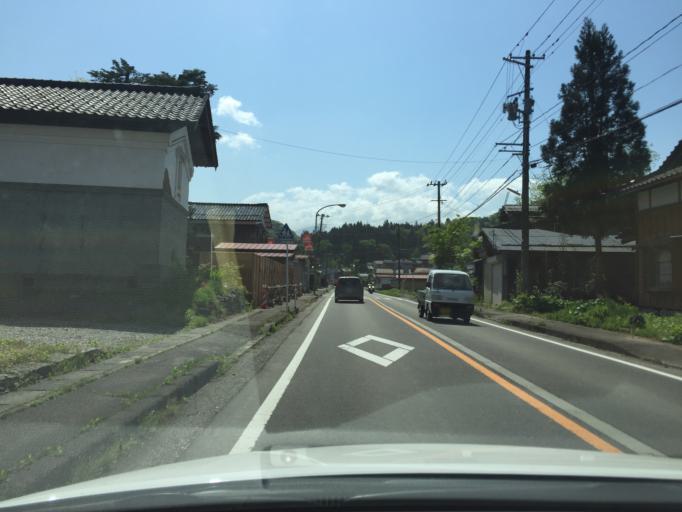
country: JP
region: Niigata
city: Kamo
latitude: 37.6283
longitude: 139.0977
